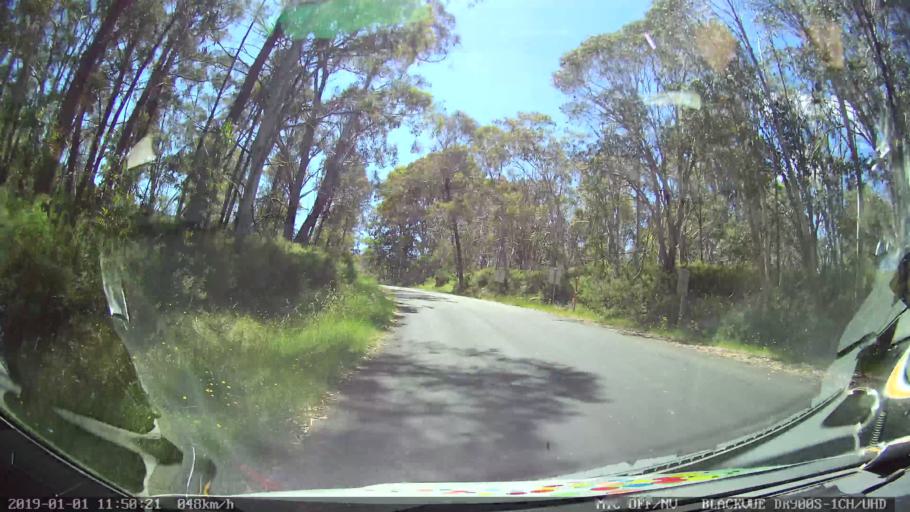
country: AU
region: New South Wales
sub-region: Snowy River
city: Jindabyne
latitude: -35.8907
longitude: 148.4201
